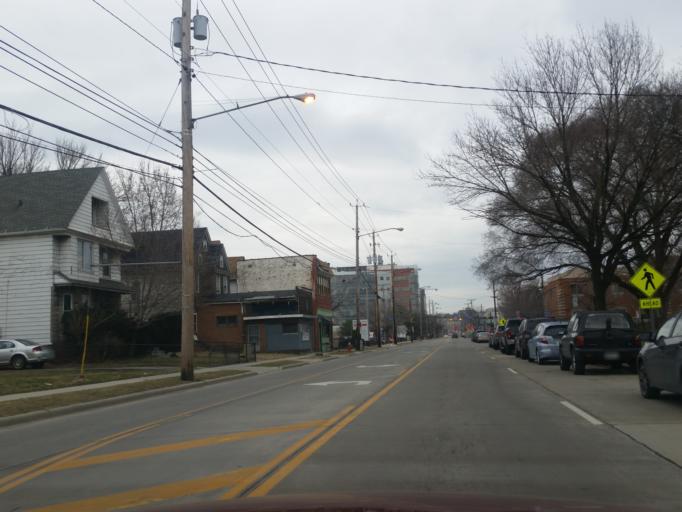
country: US
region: Ohio
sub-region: Cuyahoga County
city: Bratenahl
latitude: 41.4997
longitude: -81.6241
